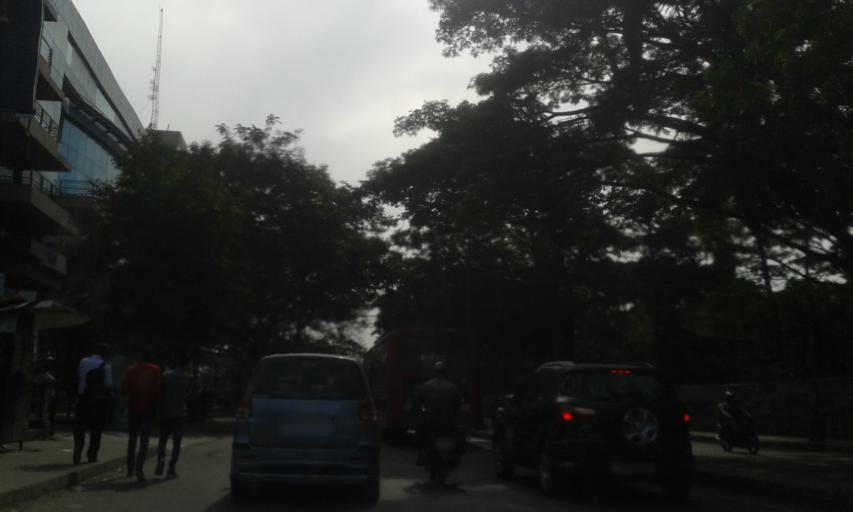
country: IN
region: Karnataka
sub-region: Bangalore Urban
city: Bangalore
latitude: 12.9334
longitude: 77.6116
